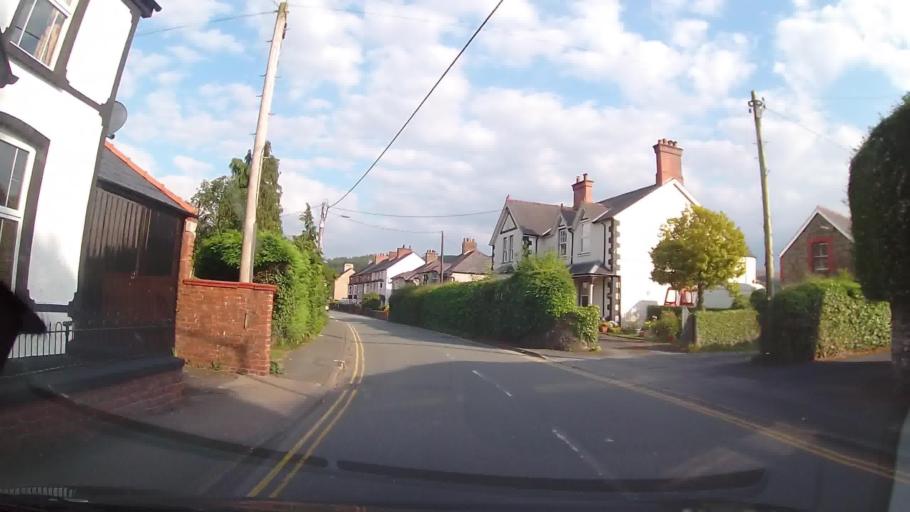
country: GB
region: Wales
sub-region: Gwynedd
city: Bala
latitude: 52.9094
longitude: -3.5972
